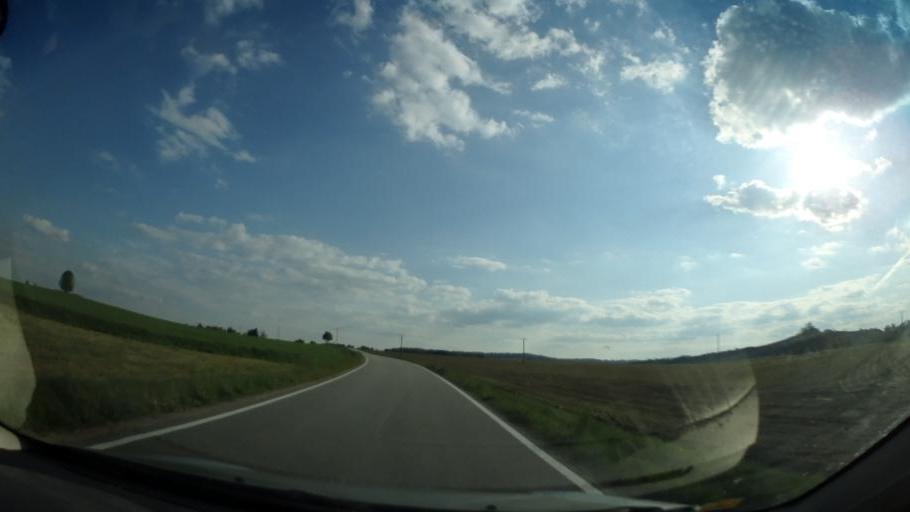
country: CZ
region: Vysocina
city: Merin
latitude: 49.3599
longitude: 15.9071
